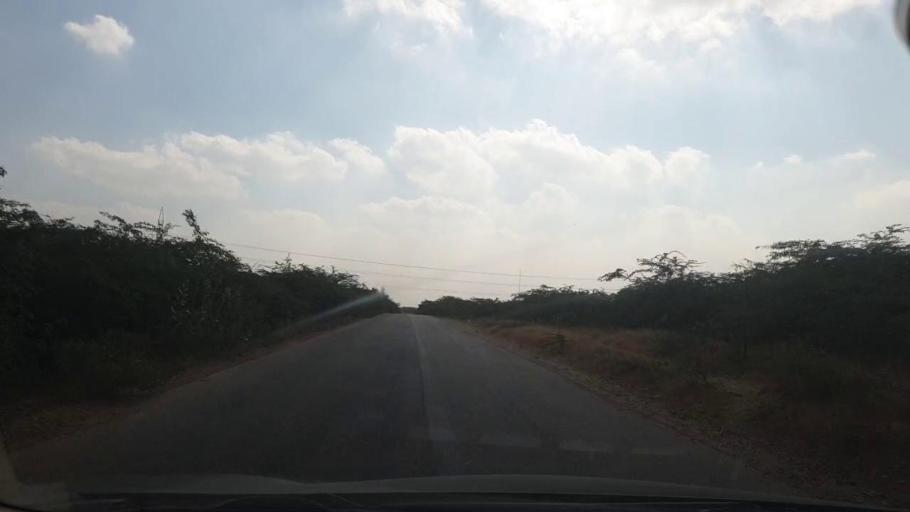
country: PK
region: Sindh
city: Malir Cantonment
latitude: 25.0124
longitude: 67.3534
